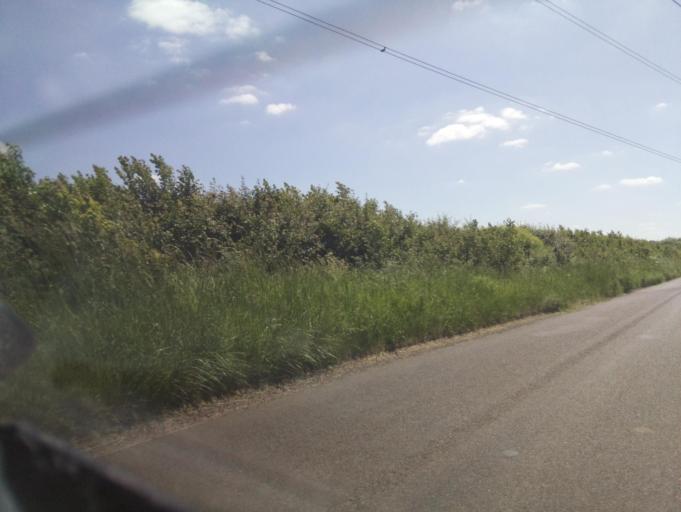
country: GB
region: England
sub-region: Wiltshire
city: Bremhill
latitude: 51.4999
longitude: -2.0736
